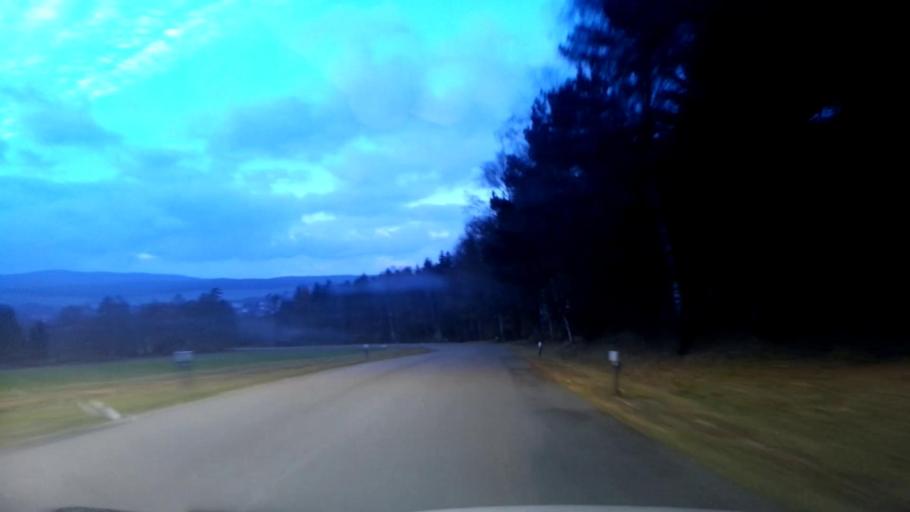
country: DE
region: Bavaria
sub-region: Upper Palatinate
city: Waldershof
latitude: 49.9709
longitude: 12.0795
